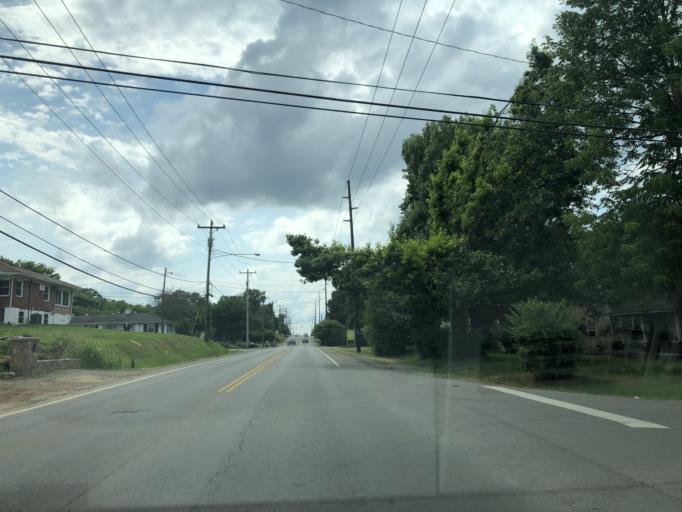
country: US
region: Tennessee
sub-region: Davidson County
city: Lakewood
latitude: 36.2628
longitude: -86.6871
